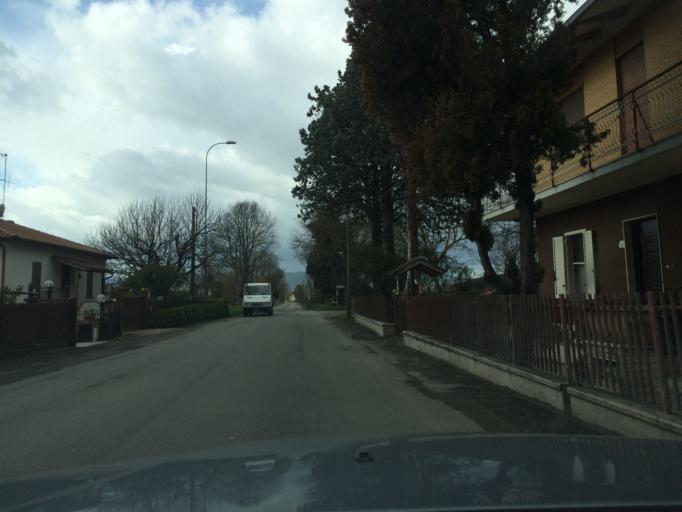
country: IT
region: Umbria
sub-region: Provincia di Terni
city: Terni
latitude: 42.5521
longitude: 12.5964
